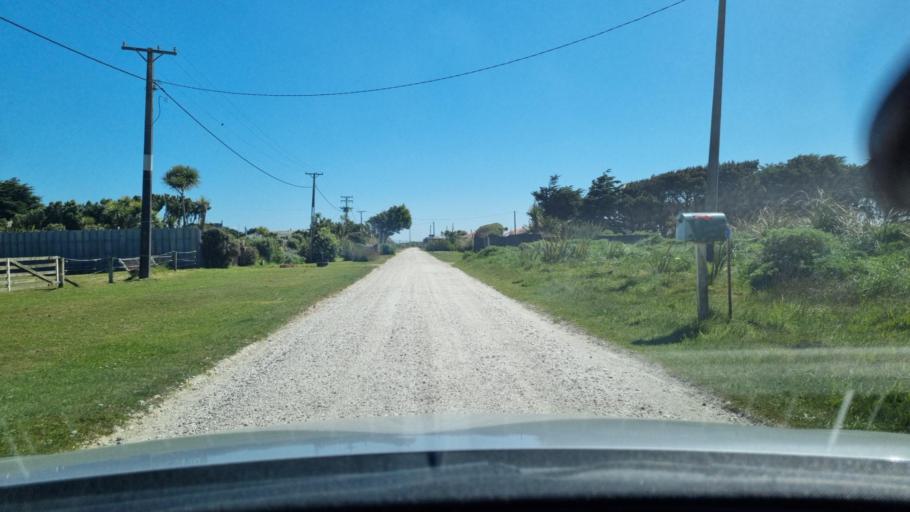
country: NZ
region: Southland
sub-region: Invercargill City
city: Invercargill
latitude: -46.4313
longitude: 168.2336
